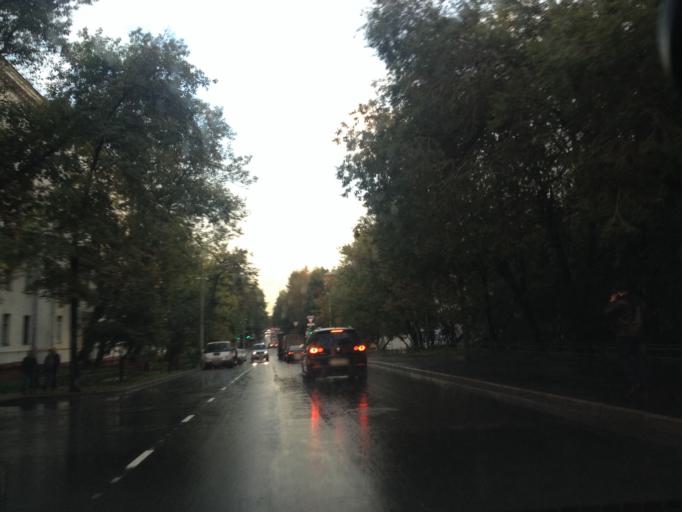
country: RU
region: Moscow
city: Metrogorodok
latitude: 55.7981
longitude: 37.7938
